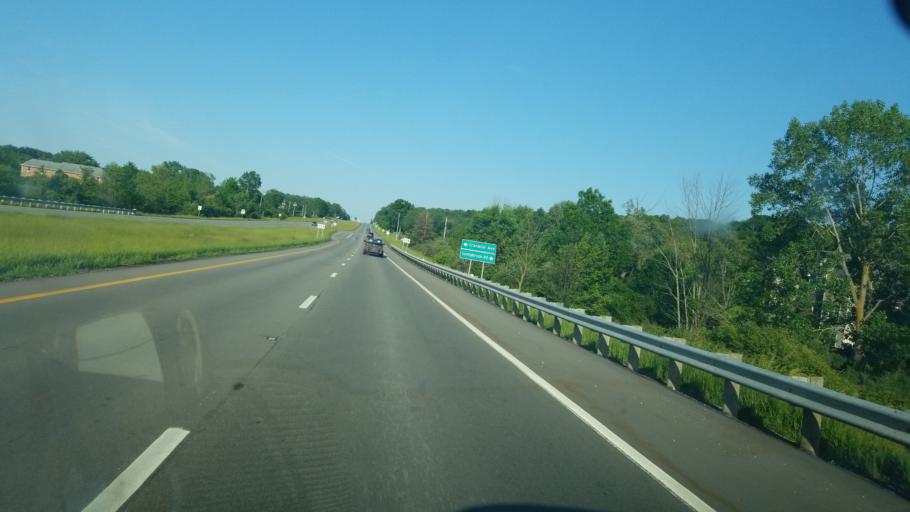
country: US
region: Ohio
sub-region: Portage County
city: Kent
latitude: 41.1344
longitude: -81.3651
